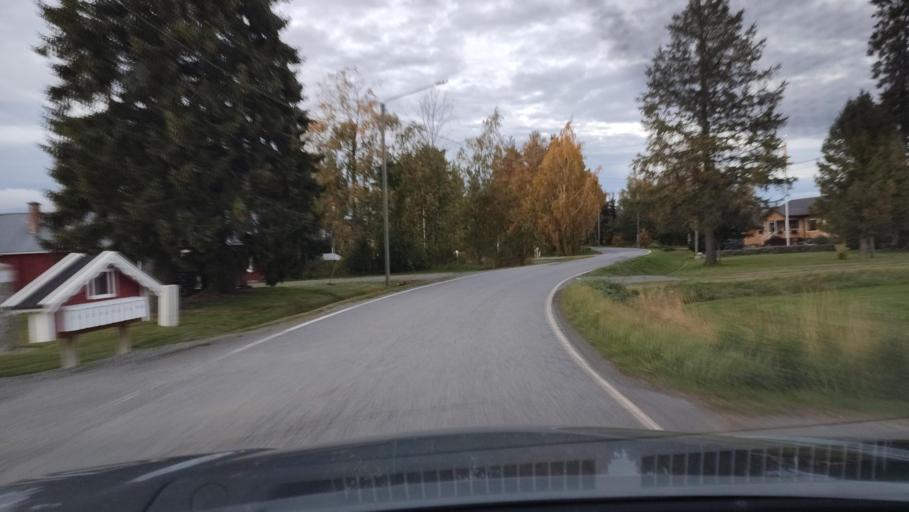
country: FI
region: Ostrobothnia
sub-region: Sydosterbotten
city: Kristinestad
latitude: 62.2616
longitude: 21.5081
